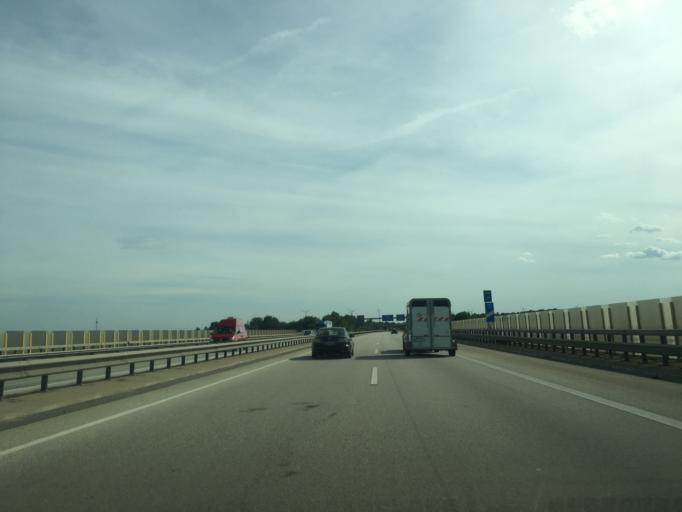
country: DE
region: Rheinland-Pfalz
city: Morstadt
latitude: 49.6321
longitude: 8.2947
